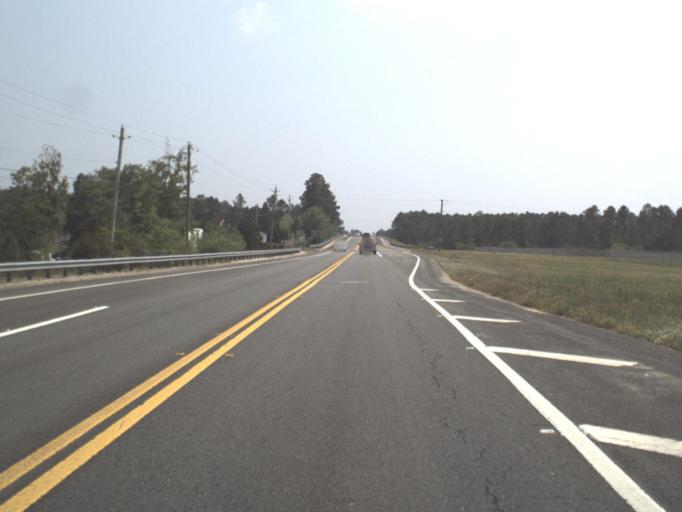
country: US
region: Florida
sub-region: Santa Rosa County
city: Bagdad
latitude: 30.5278
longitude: -87.0873
